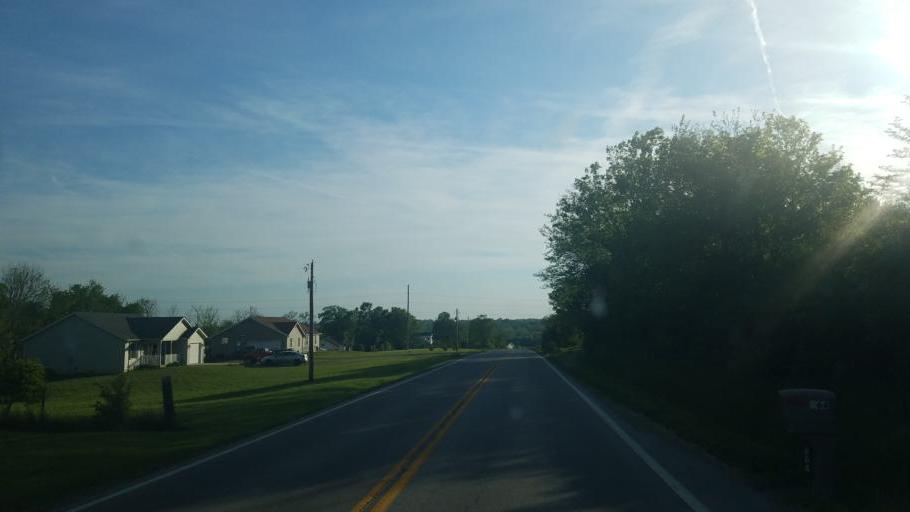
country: US
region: Ohio
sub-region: Highland County
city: Greenfield
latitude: 39.3635
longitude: -83.3682
